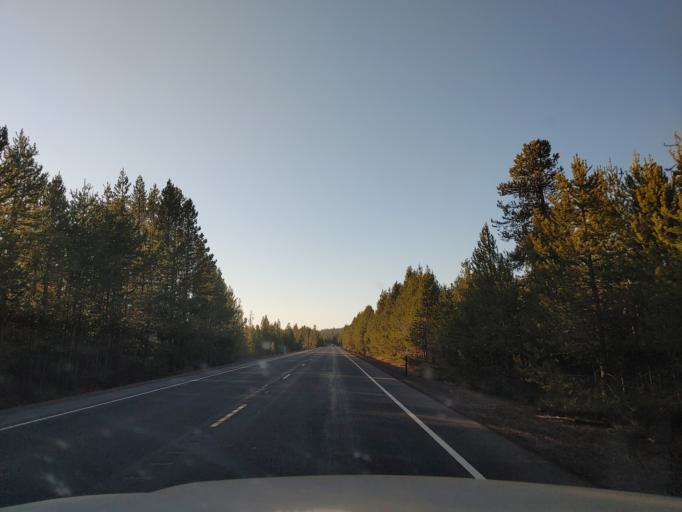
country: US
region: Oregon
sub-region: Deschutes County
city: La Pine
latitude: 43.4151
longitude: -121.8356
